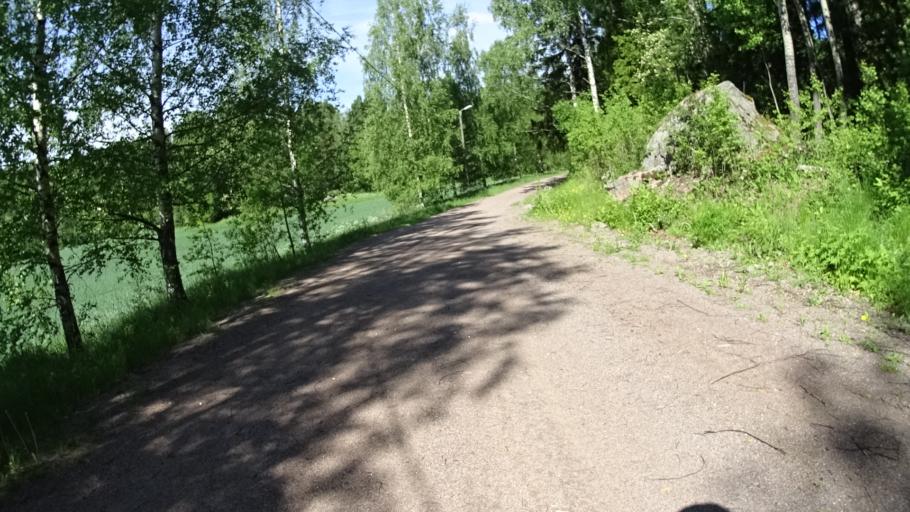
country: FI
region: Uusimaa
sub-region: Helsinki
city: Kilo
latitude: 60.2945
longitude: 24.8070
